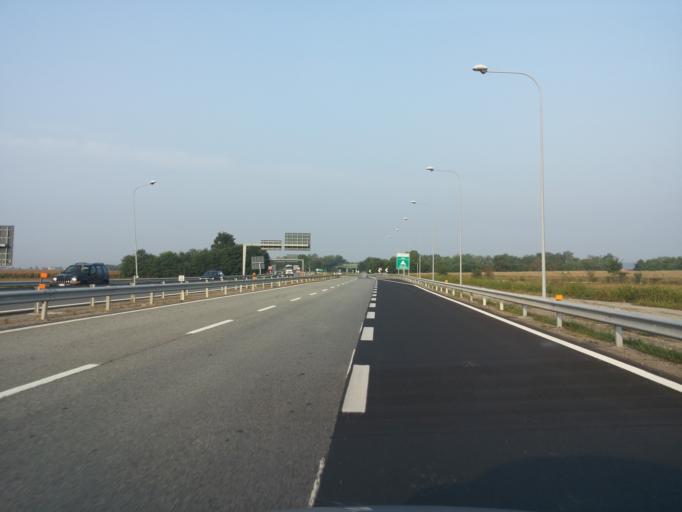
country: IT
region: Piedmont
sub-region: Provincia di Biella
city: Cavaglia
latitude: 45.3726
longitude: 8.1224
